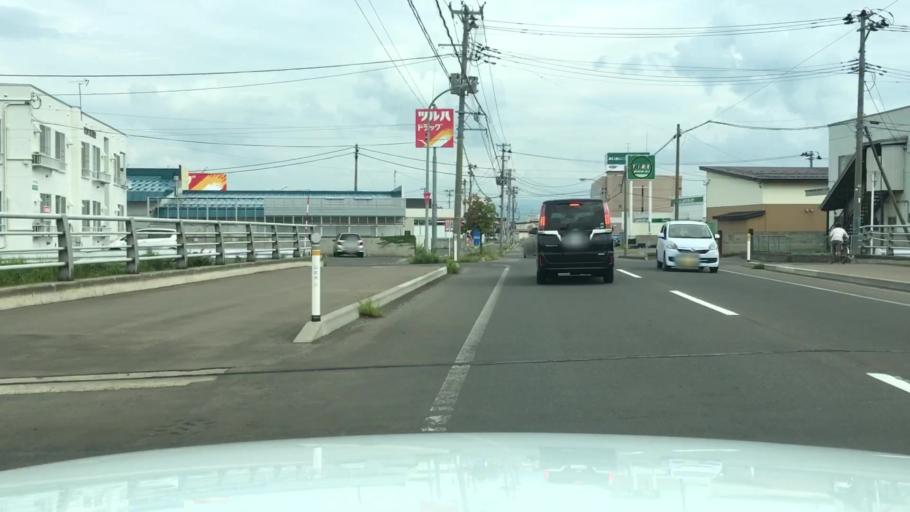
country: JP
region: Aomori
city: Hirosaki
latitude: 40.6157
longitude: 140.4884
